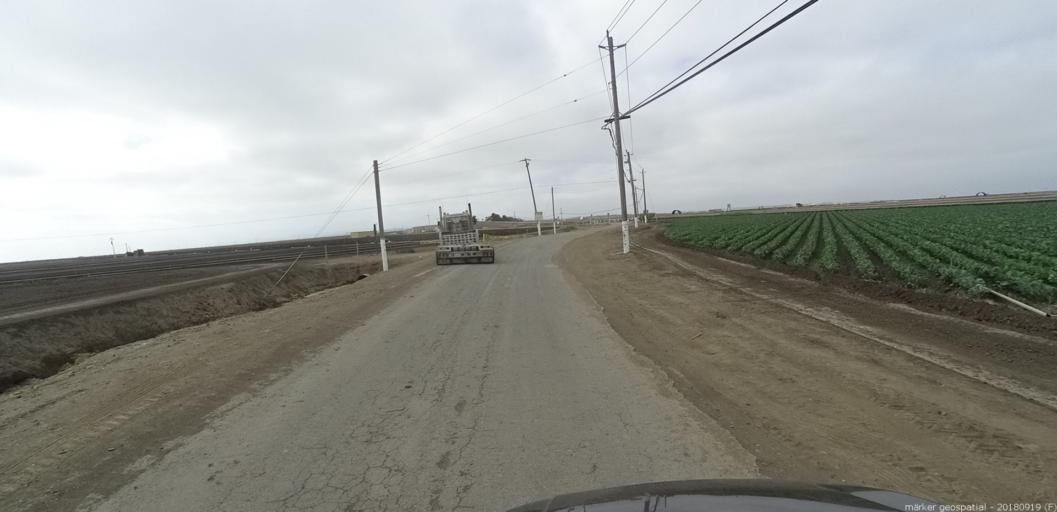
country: US
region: California
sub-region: Monterey County
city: Castroville
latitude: 36.7599
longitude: -121.7641
